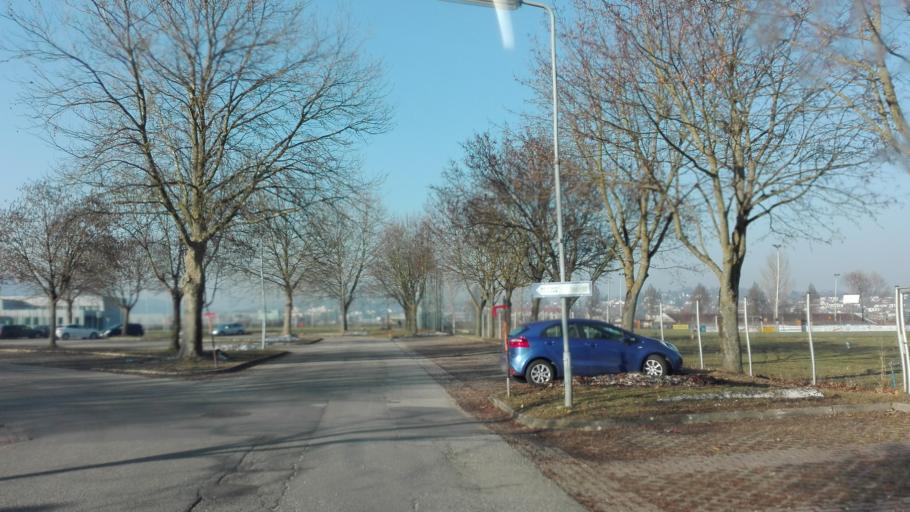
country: AT
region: Upper Austria
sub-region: Politischer Bezirk Linz-Land
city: Leonding
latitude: 48.2672
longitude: 14.2543
